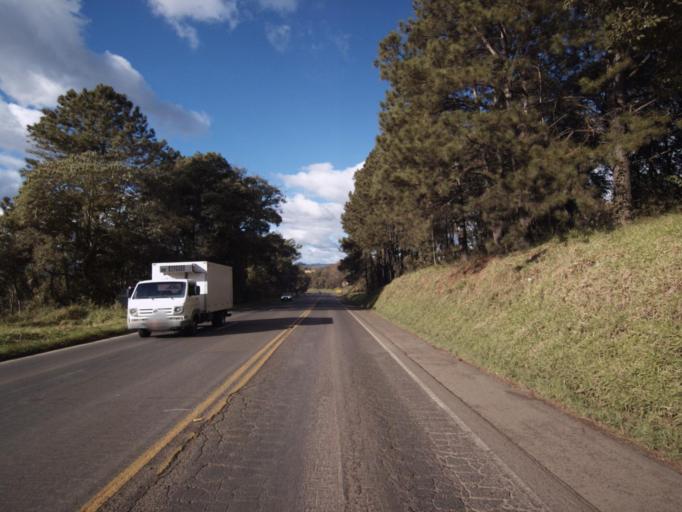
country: BR
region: Santa Catarina
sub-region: Joacaba
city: Joacaba
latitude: -27.1798
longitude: -51.5351
